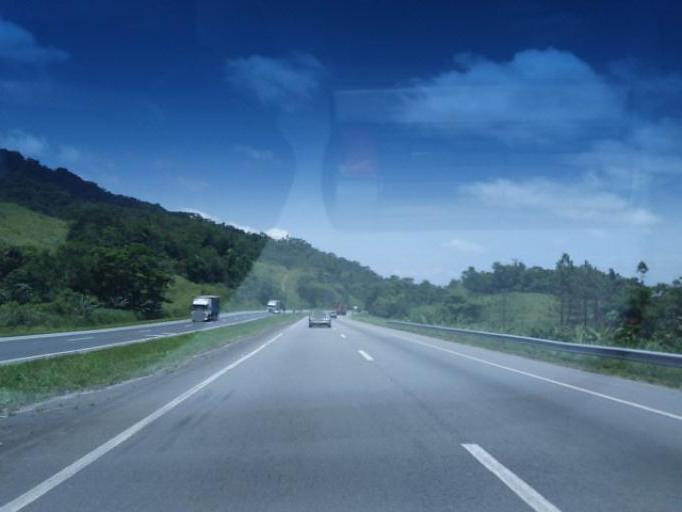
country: BR
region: Sao Paulo
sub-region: Miracatu
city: Miracatu
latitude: -24.3053
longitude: -47.4913
